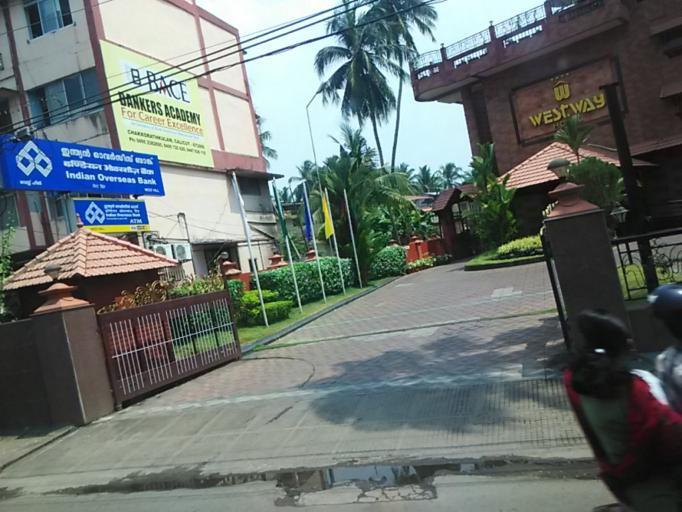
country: IN
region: Kerala
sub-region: Kozhikode
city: Kozhikode
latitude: 11.2766
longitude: 75.7719
